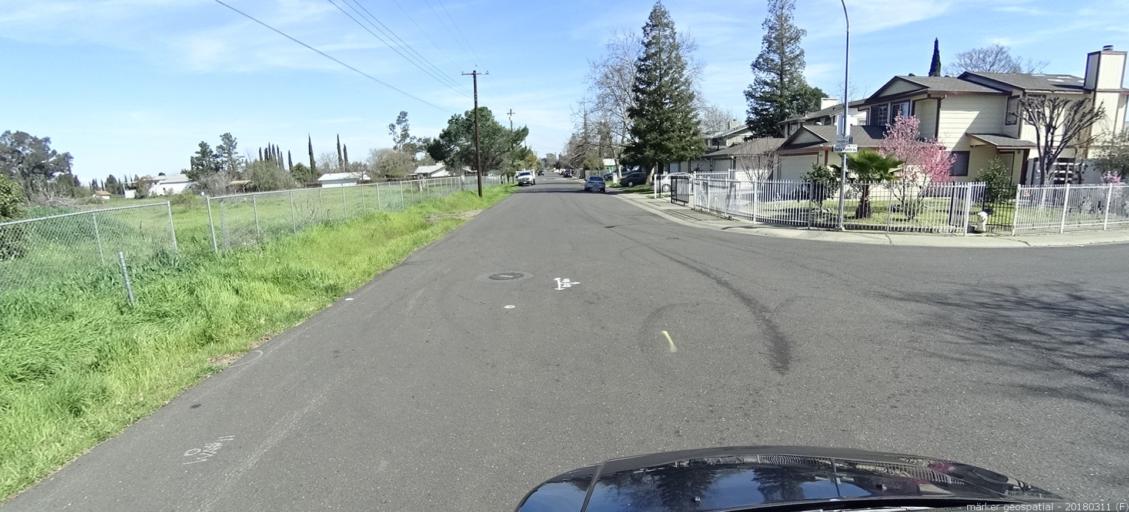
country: US
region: California
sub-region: Sacramento County
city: Florin
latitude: 38.4852
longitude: -121.4330
